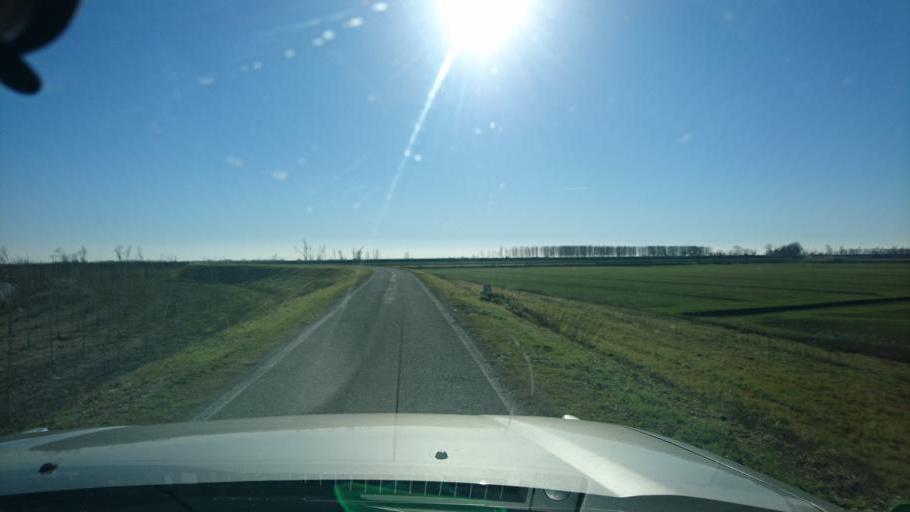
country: IT
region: Veneto
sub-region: Provincia di Rovigo
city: Ariano
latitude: 44.9360
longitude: 12.1577
